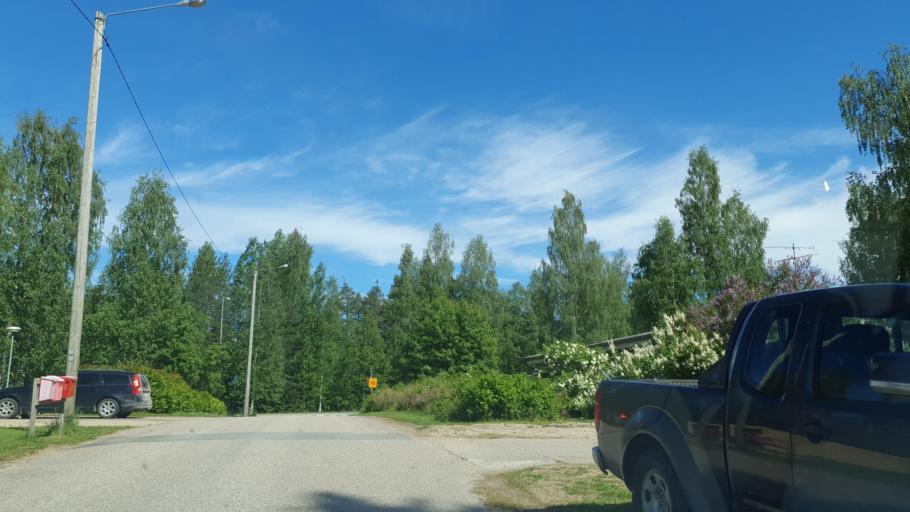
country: FI
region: Kainuu
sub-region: Kehys-Kainuu
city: Hyrynsalmi
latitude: 64.6823
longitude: 28.4658
